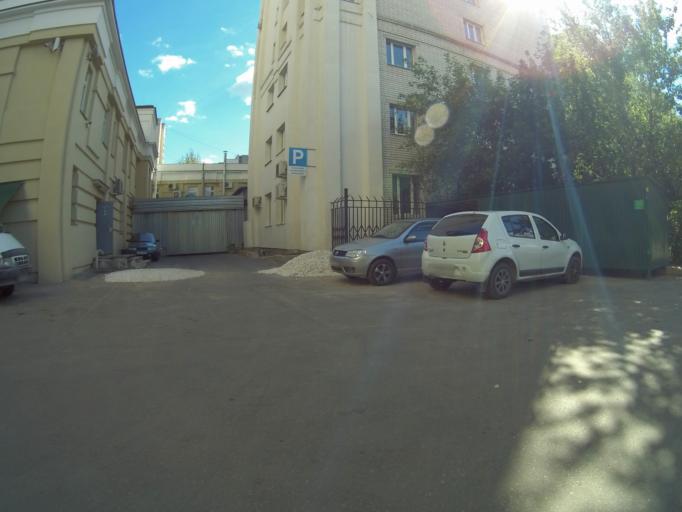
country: RU
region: Vladimir
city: Vladimir
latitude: 56.1201
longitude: 40.3612
